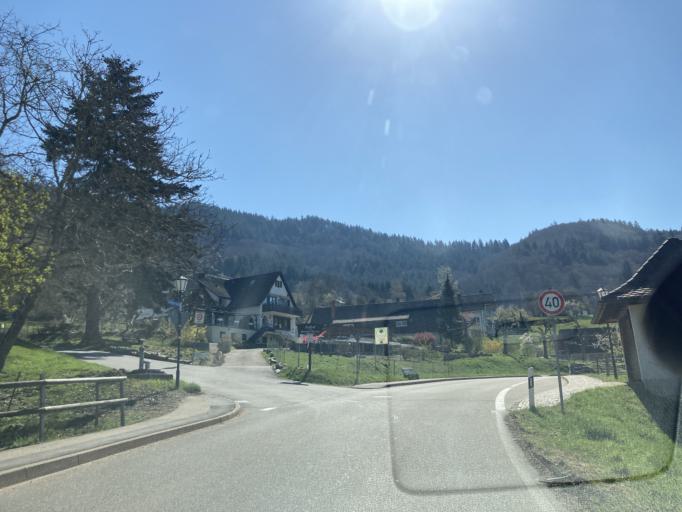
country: DE
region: Baden-Wuerttemberg
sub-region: Freiburg Region
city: Badenweiler
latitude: 47.7814
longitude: 7.6745
